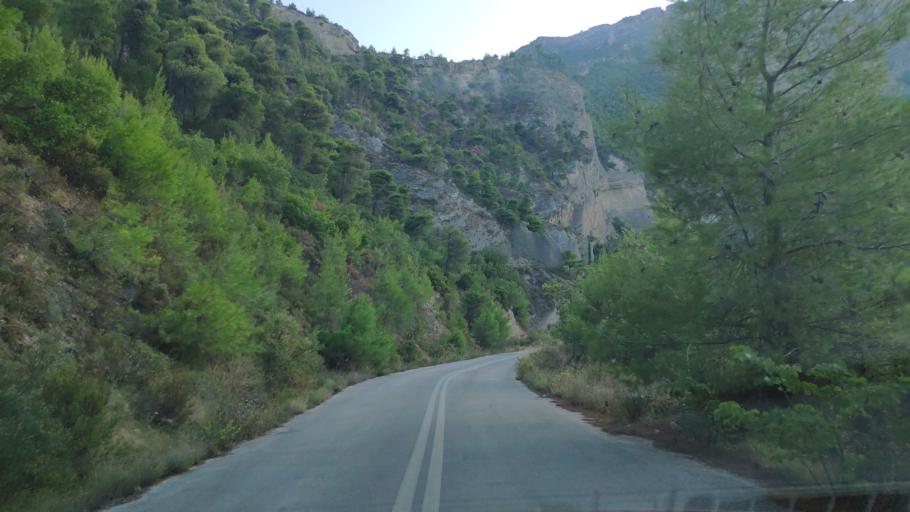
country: GR
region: West Greece
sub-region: Nomos Achaias
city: Aiyira
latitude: 38.0970
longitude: 22.4061
